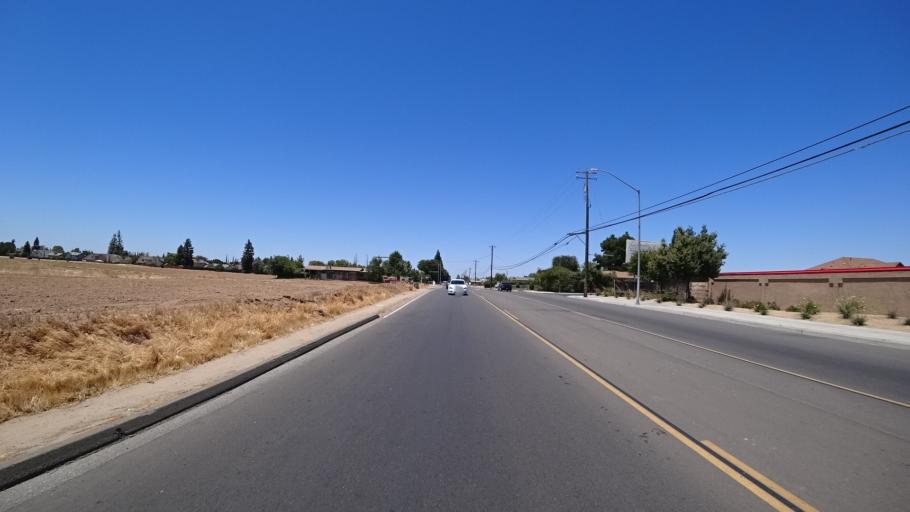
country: US
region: California
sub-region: Fresno County
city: West Park
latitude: 36.7719
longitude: -119.8469
